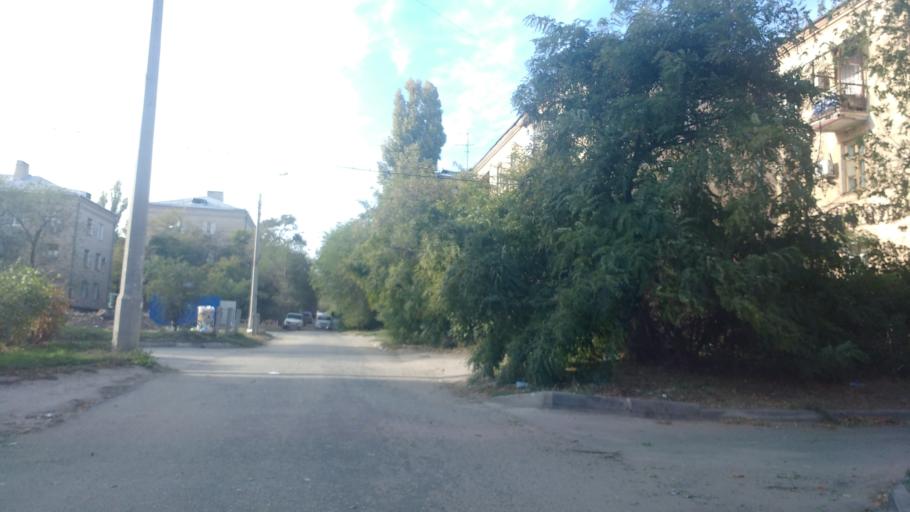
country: RU
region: Volgograd
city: Krasnoslobodsk
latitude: 48.7657
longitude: 44.5567
